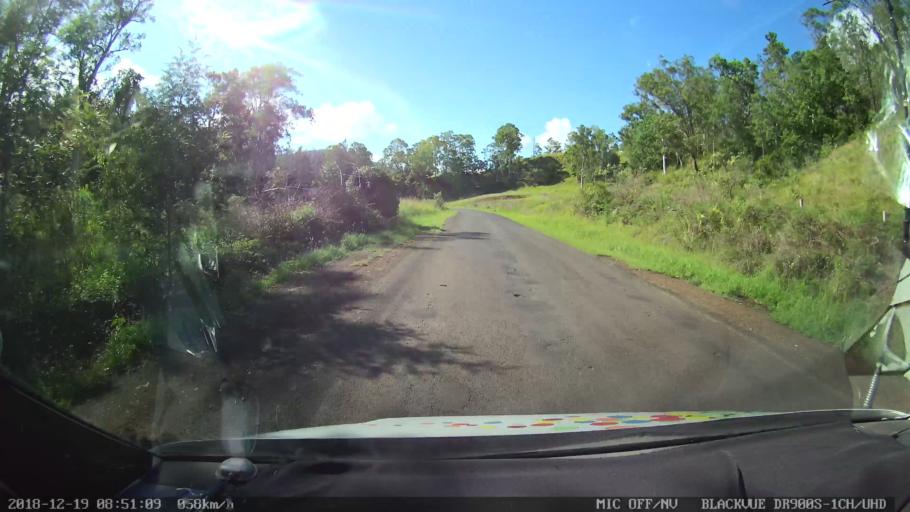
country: AU
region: New South Wales
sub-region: Kyogle
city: Kyogle
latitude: -28.3863
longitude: 152.9773
